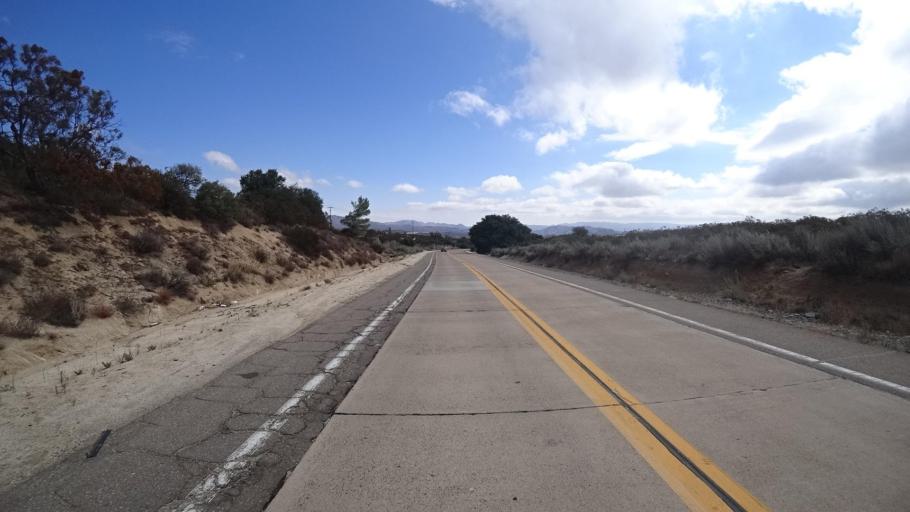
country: US
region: California
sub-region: San Diego County
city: Campo
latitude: 32.6694
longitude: -116.3112
